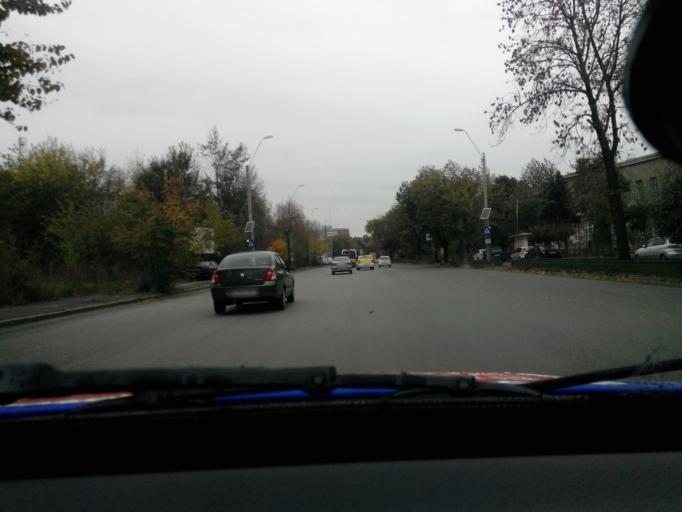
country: RO
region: Bucuresti
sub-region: Municipiul Bucuresti
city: Bucuresti
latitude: 44.4294
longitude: 26.0623
